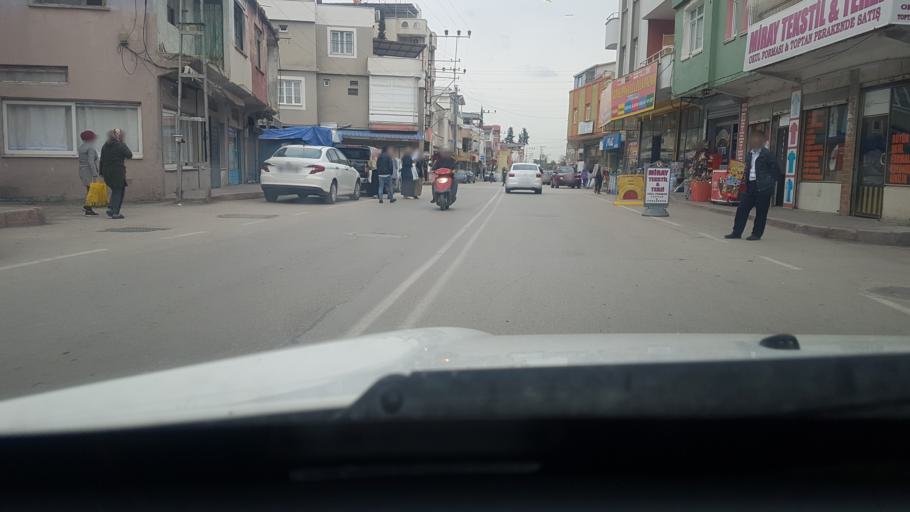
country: TR
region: Adana
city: Seyhan
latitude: 37.0144
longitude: 35.2771
